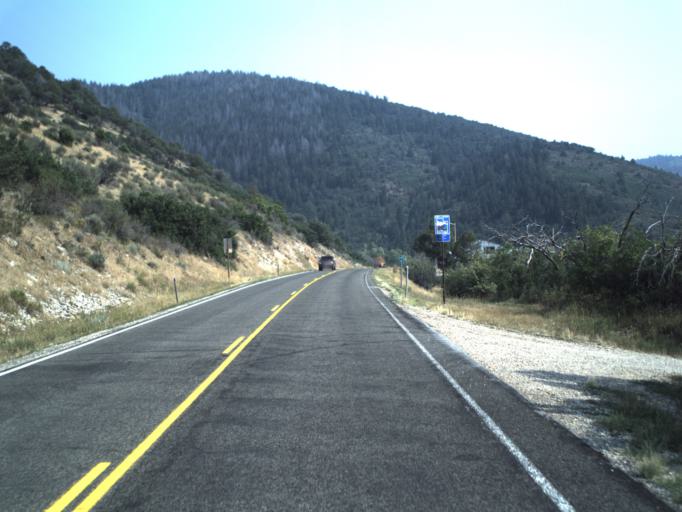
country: US
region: Utah
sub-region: Summit County
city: Francis
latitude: 40.6189
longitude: -111.2163
